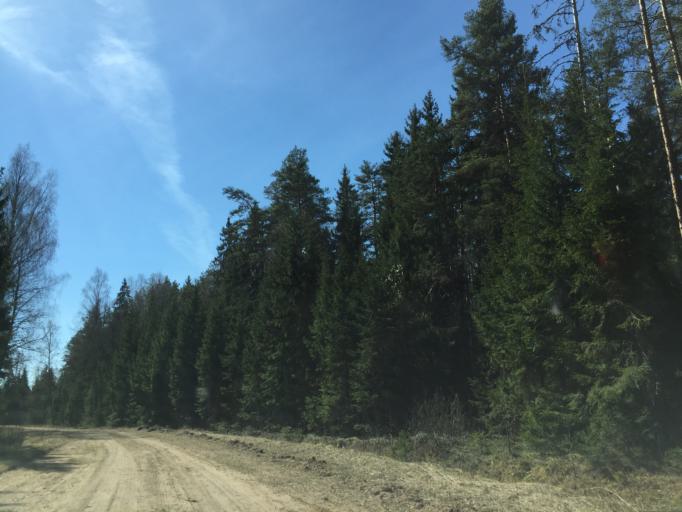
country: LV
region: Strenci
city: Seda
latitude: 57.6392
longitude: 25.8378
